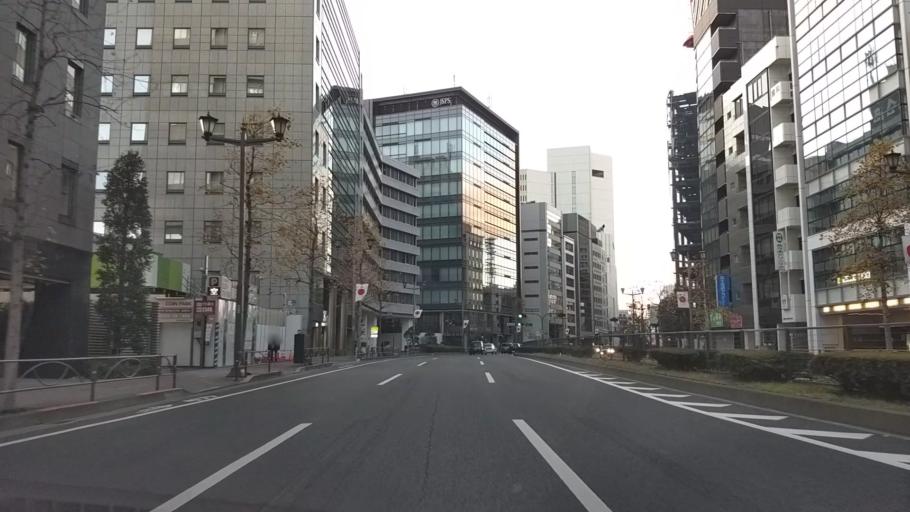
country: JP
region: Tokyo
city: Tokyo
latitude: 35.6839
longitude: 139.7359
